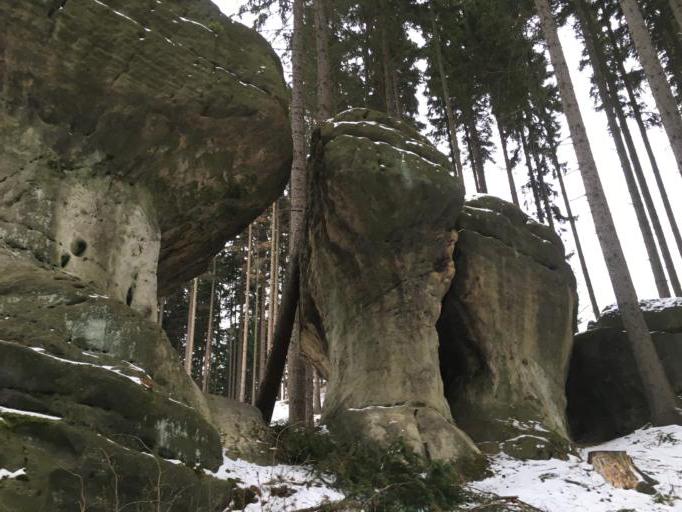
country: PL
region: Lower Silesian Voivodeship
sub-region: Powiat kamiennogorski
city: Krzeszow
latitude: 50.6963
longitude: 16.0980
